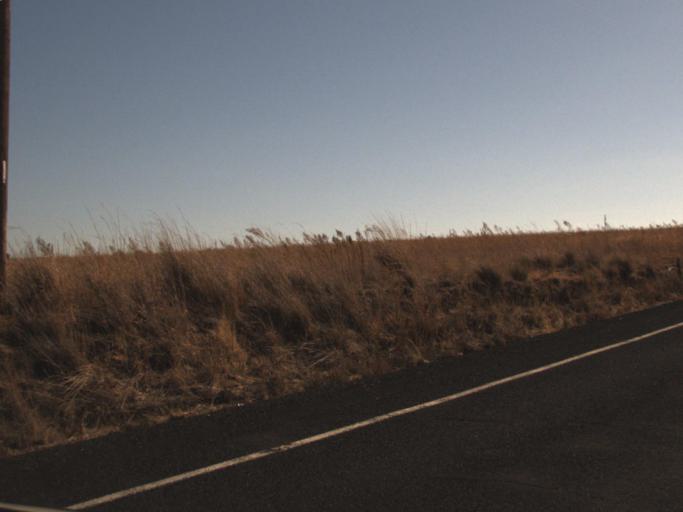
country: US
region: Washington
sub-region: Adams County
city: Ritzville
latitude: 47.0755
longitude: -118.6629
